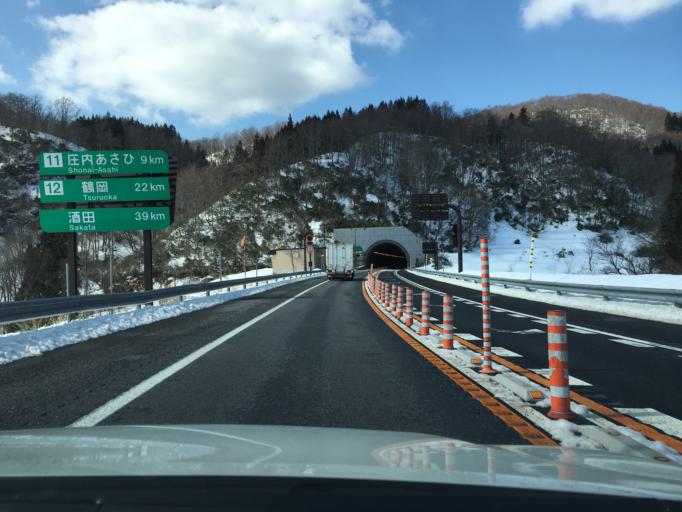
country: JP
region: Yamagata
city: Tsuruoka
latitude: 38.5725
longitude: 139.9120
